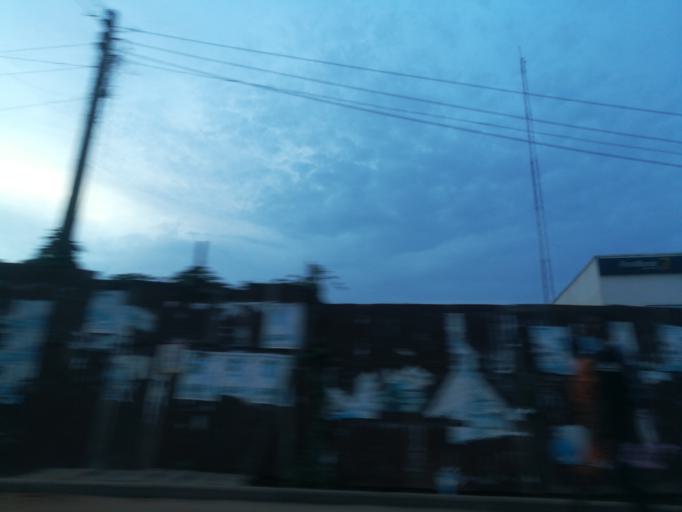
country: NG
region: Oyo
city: Ibadan
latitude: 7.3912
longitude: 3.9034
